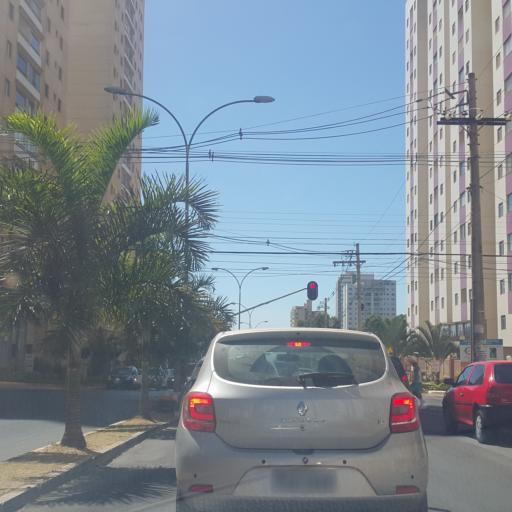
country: BR
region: Federal District
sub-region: Brasilia
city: Brasilia
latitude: -15.8392
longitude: -48.0369
